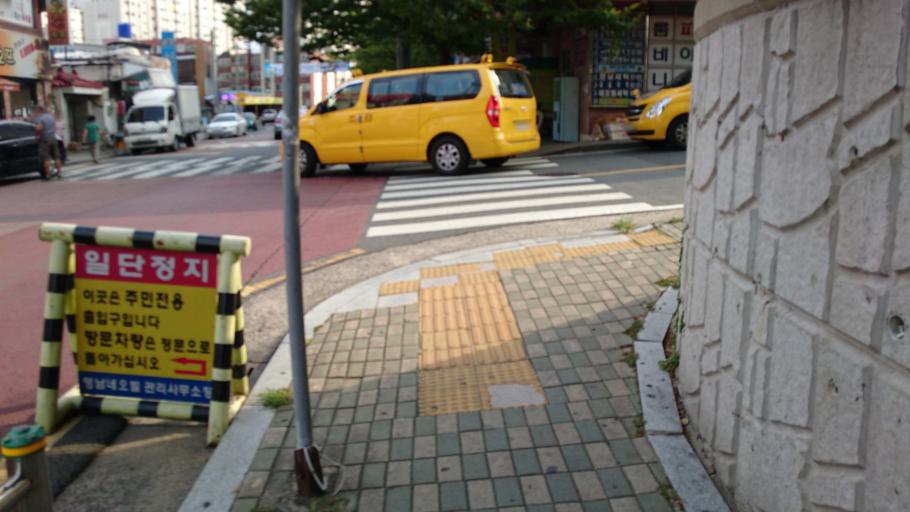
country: KR
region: Daegu
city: Daegu
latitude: 35.8812
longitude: 128.6617
